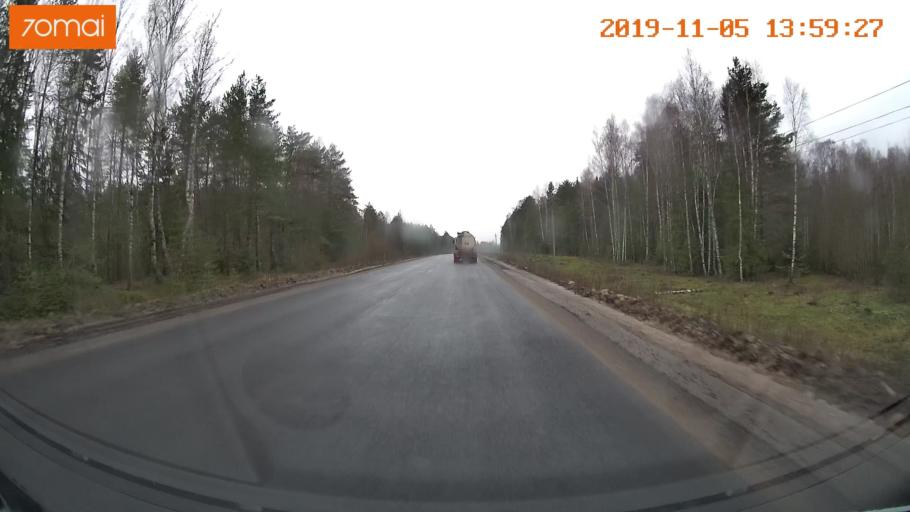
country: RU
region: Ivanovo
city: Kitovo
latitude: 57.0182
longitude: 41.2685
